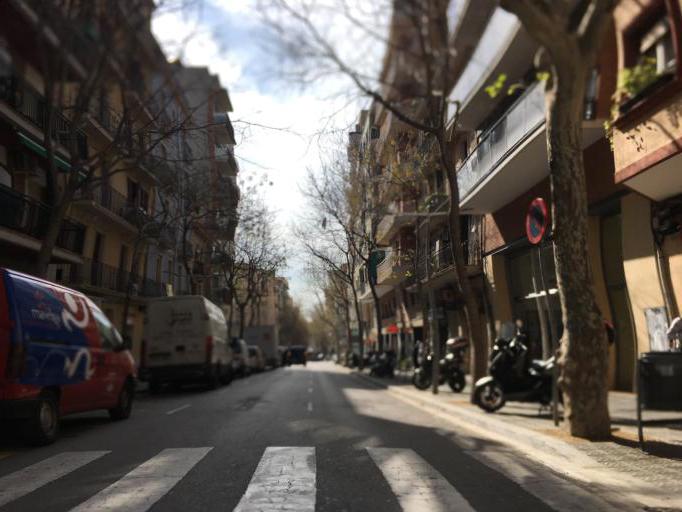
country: ES
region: Catalonia
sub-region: Provincia de Barcelona
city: les Corts
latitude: 41.3826
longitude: 2.1350
